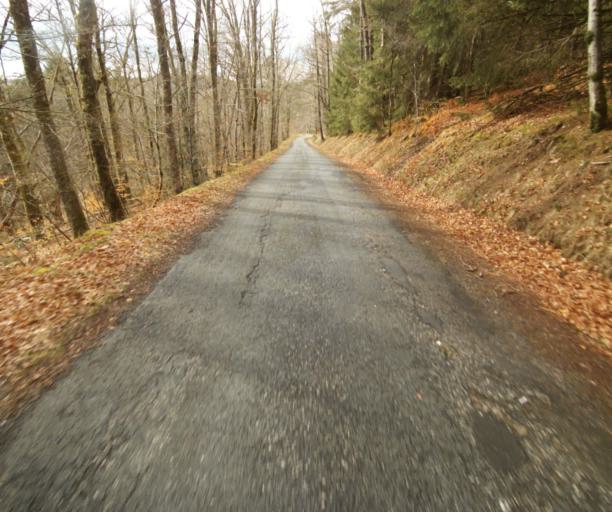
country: FR
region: Limousin
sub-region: Departement de la Correze
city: Saint-Privat
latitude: 45.2459
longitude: 1.9991
